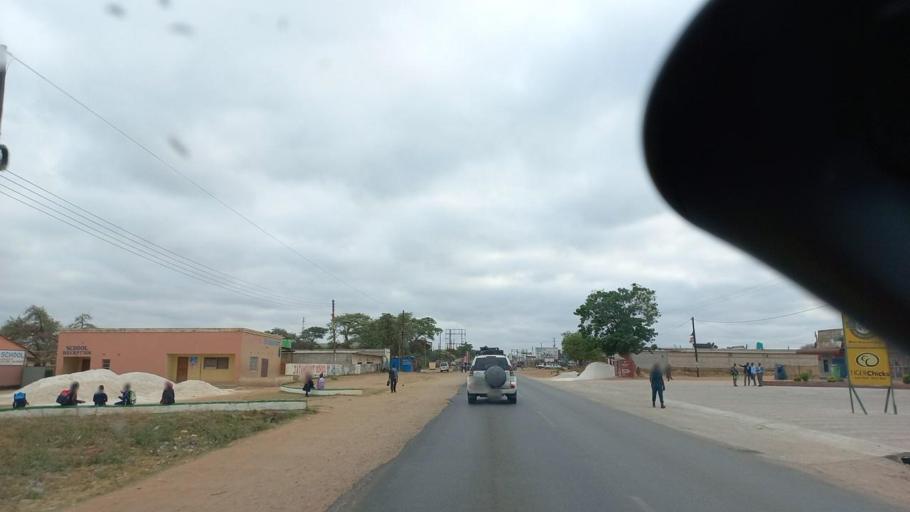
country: ZM
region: Lusaka
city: Chongwe
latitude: -15.3338
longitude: 28.6724
